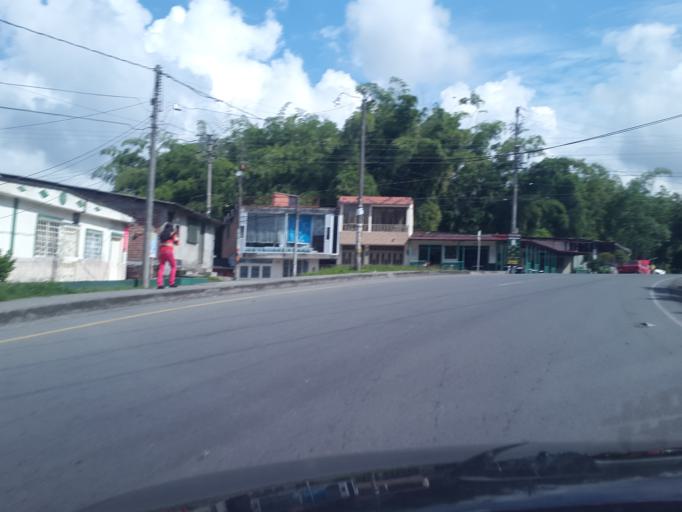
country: CO
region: Quindio
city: Calarca
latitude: 4.5326
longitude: -75.6448
